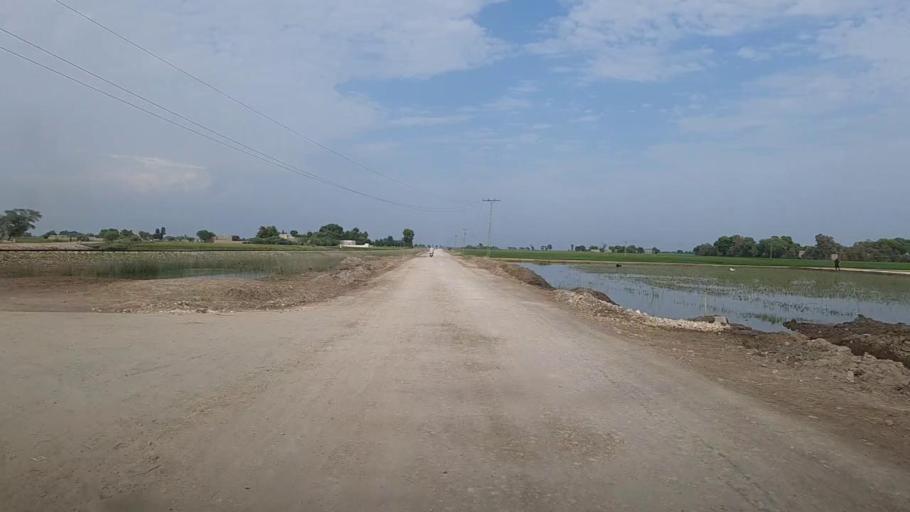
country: PK
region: Sindh
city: Thul
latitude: 28.2579
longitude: 68.8104
